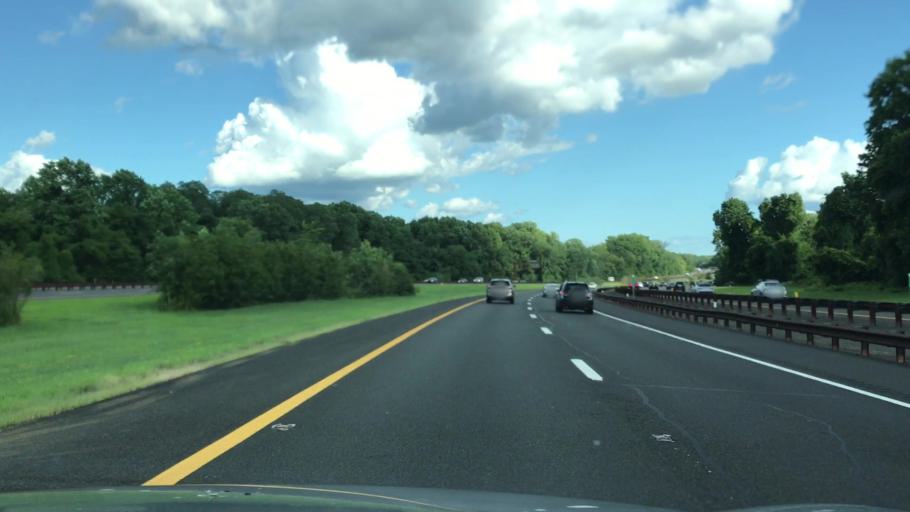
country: US
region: New Jersey
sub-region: Monmouth County
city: Lincroft
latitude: 40.3534
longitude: -74.1207
